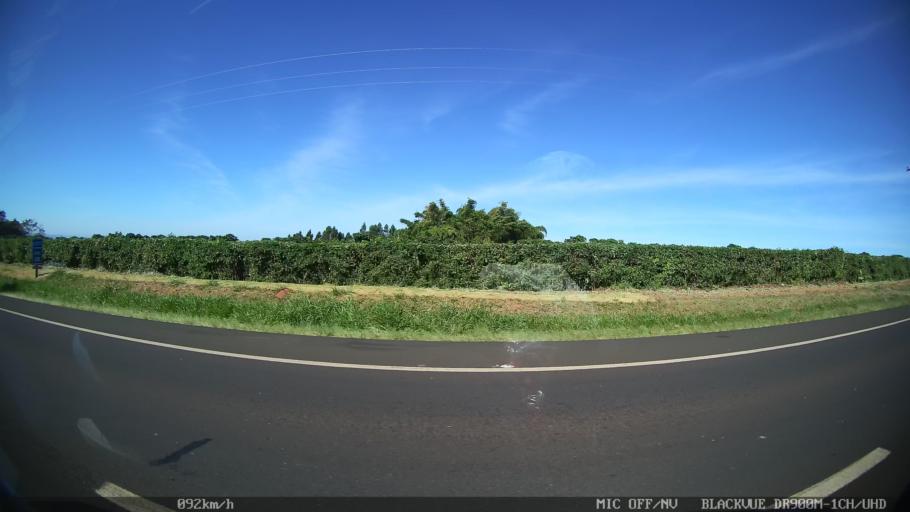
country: BR
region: Sao Paulo
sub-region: Franca
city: Franca
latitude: -20.5777
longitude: -47.3472
